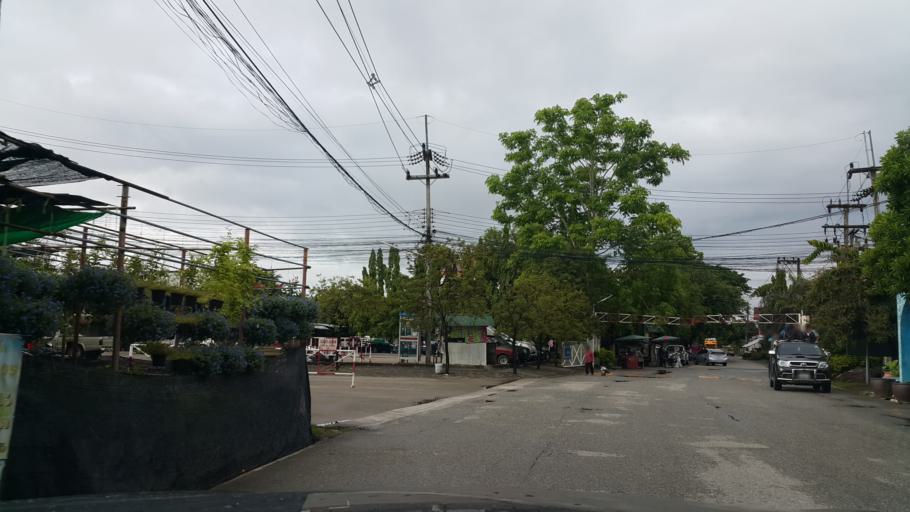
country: TH
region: Chiang Mai
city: Chiang Mai
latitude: 18.8053
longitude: 98.9973
